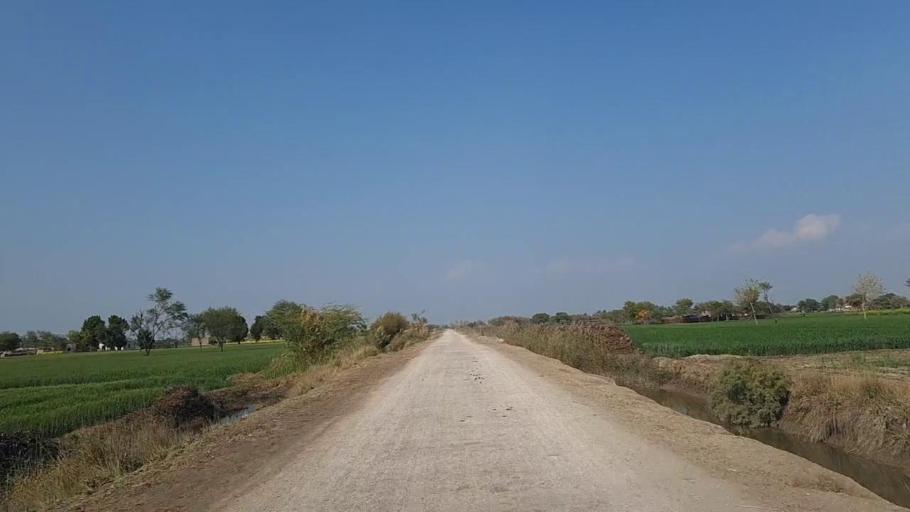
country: PK
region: Sindh
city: Jam Sahib
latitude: 26.2927
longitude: 68.5831
